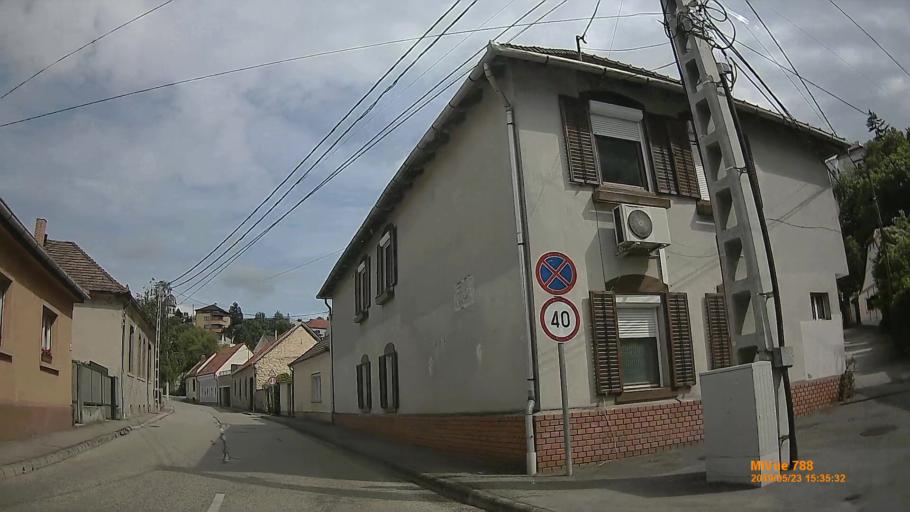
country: HU
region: Veszprem
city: Veszprem
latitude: 47.0963
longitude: 17.9060
